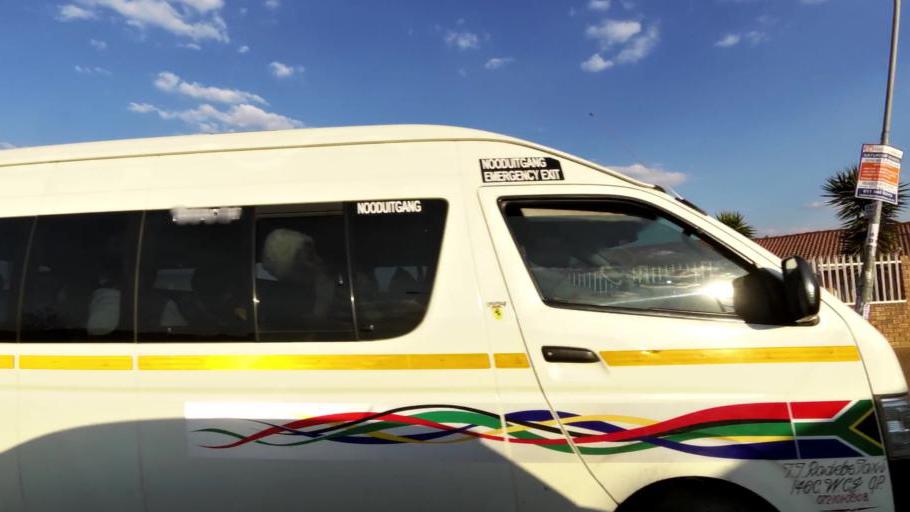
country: ZA
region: Gauteng
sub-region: City of Johannesburg Metropolitan Municipality
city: Soweto
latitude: -26.2200
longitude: 27.9015
